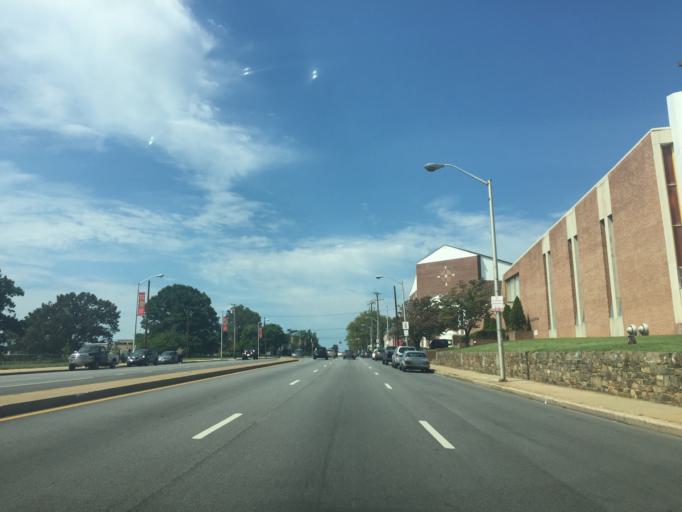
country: US
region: Maryland
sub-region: Baltimore County
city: Charlestown
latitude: 39.2937
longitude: -76.6870
